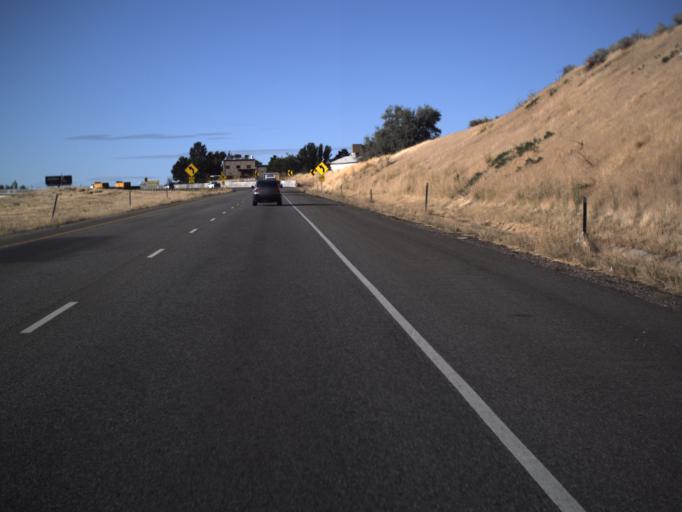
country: US
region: Utah
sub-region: Weber County
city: Riverdale
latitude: 41.1888
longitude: -112.0084
